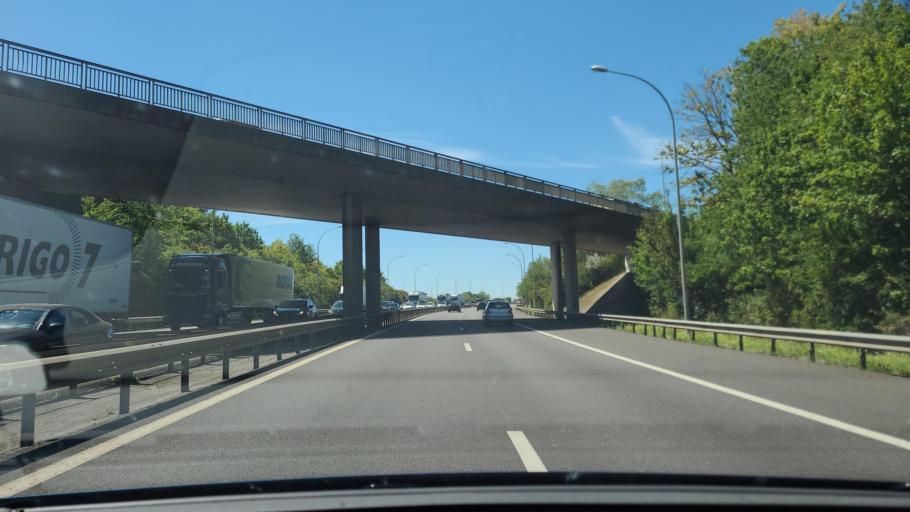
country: LU
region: Luxembourg
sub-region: Canton d'Esch-sur-Alzette
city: Leudelange
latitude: 49.5674
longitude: 6.0857
